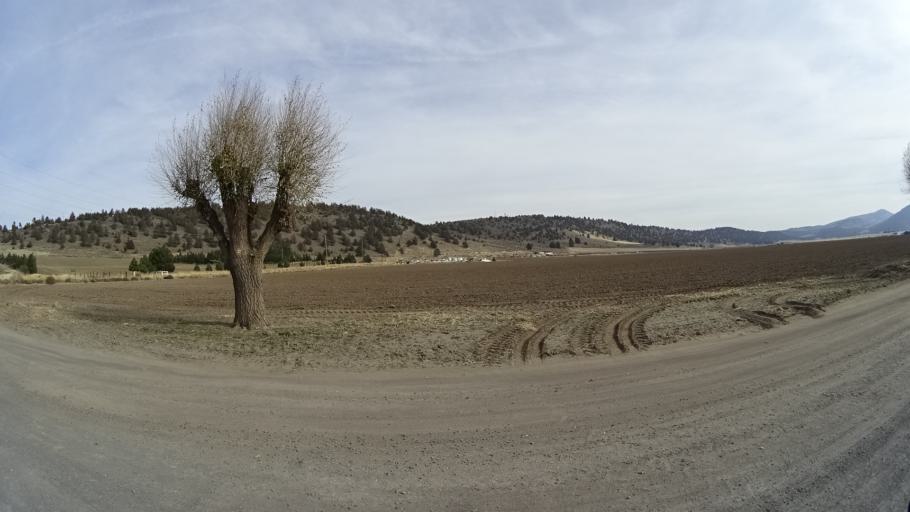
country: US
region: Oregon
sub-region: Klamath County
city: Klamath Falls
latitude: 41.9664
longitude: -121.9115
